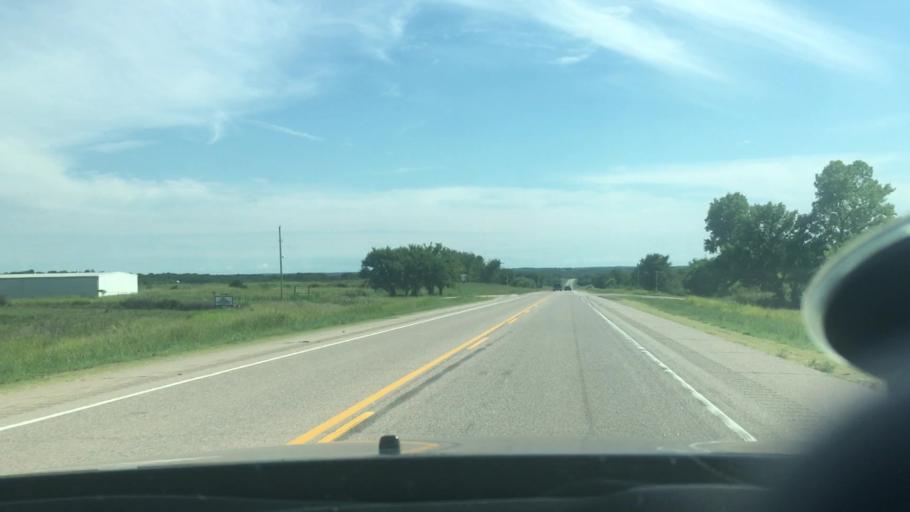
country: US
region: Oklahoma
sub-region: Seminole County
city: Maud
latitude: 35.0882
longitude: -96.6788
